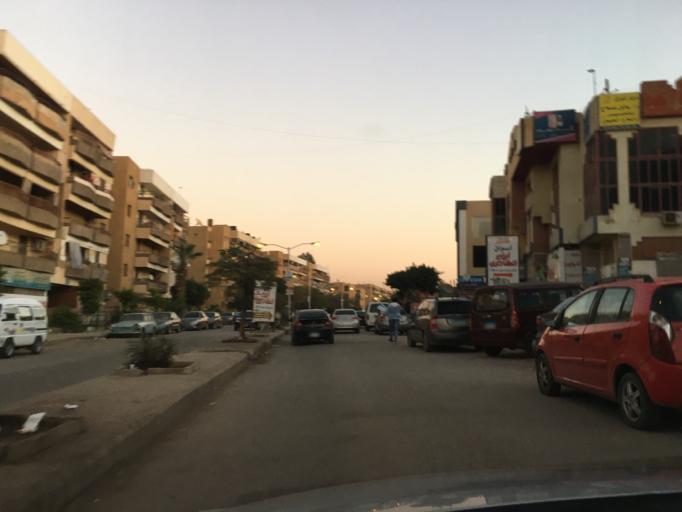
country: EG
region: Al Jizah
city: Madinat Sittah Uktubar
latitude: 29.9831
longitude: 30.9396
